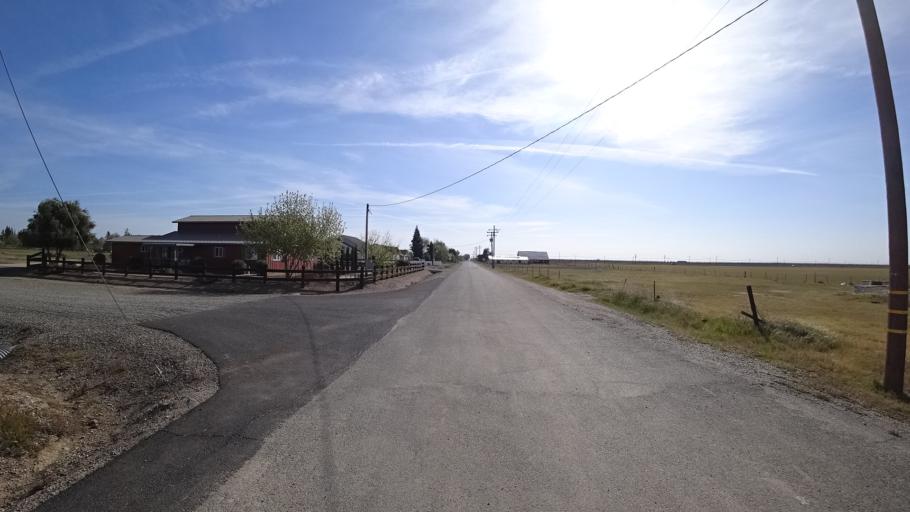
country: US
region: California
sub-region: Glenn County
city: Willows
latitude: 39.6114
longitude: -122.1981
